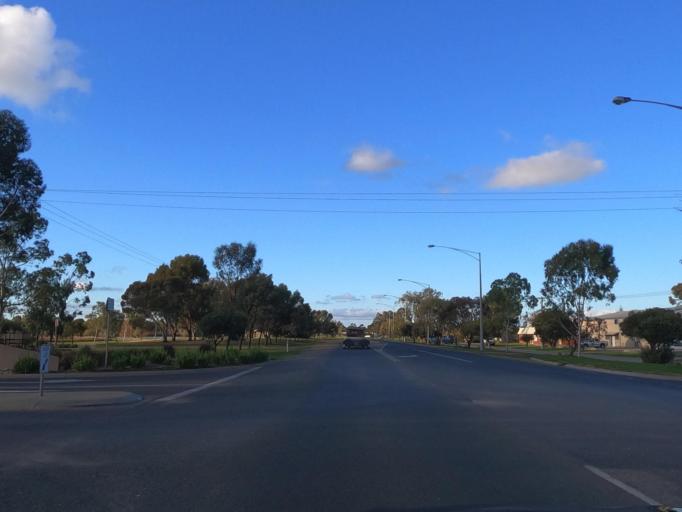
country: AU
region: Victoria
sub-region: Swan Hill
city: Swan Hill
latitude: -35.3416
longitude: 143.5354
